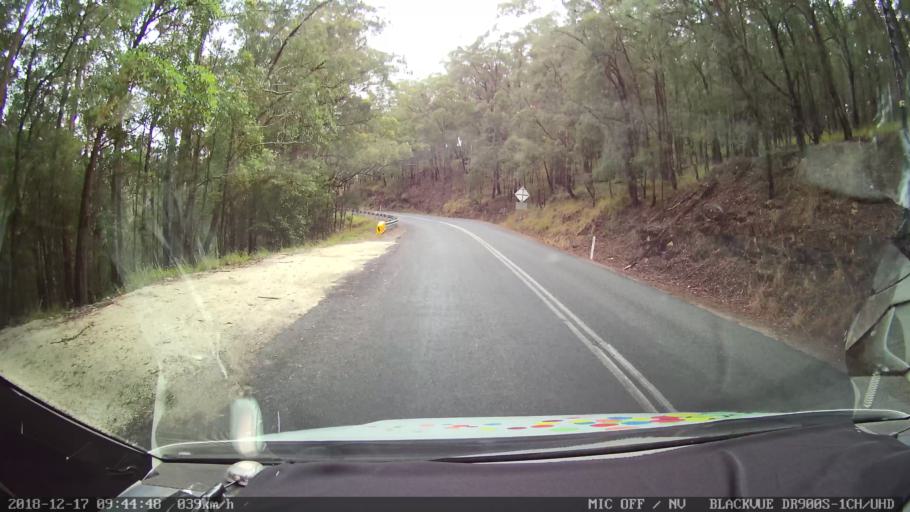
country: AU
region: New South Wales
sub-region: Tenterfield Municipality
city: Carrolls Creek
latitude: -28.9276
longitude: 152.3250
